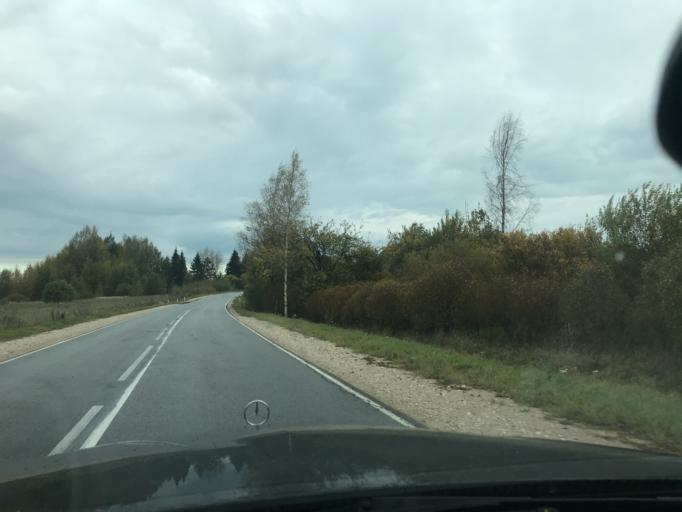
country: RU
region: Pskov
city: Izborsk
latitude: 57.6502
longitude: 27.8956
